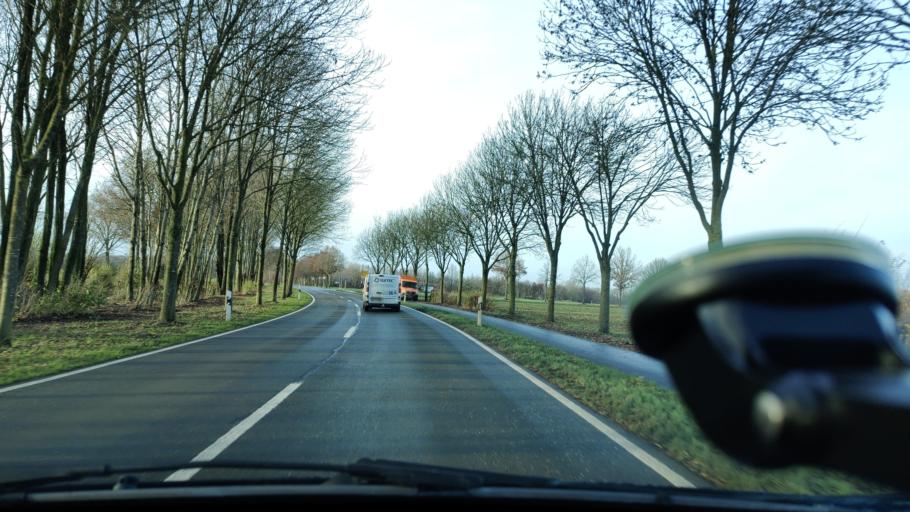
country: DE
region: North Rhine-Westphalia
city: Kalkar
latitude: 51.7539
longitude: 6.3095
